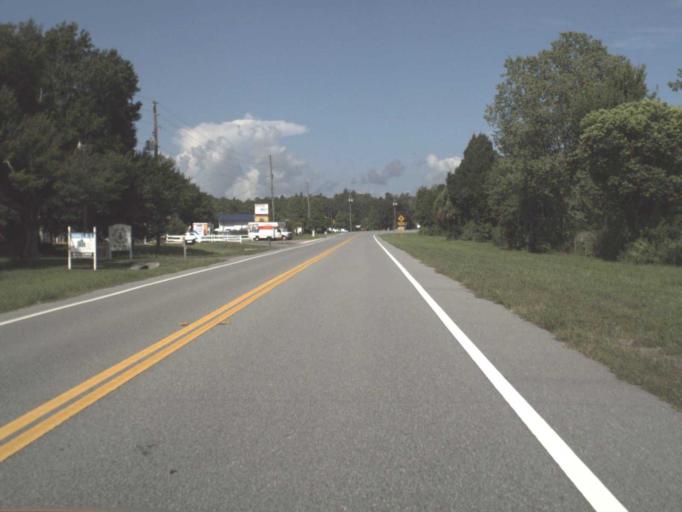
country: US
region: Florida
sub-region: Pasco County
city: Odessa
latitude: 28.1902
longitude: -82.5732
